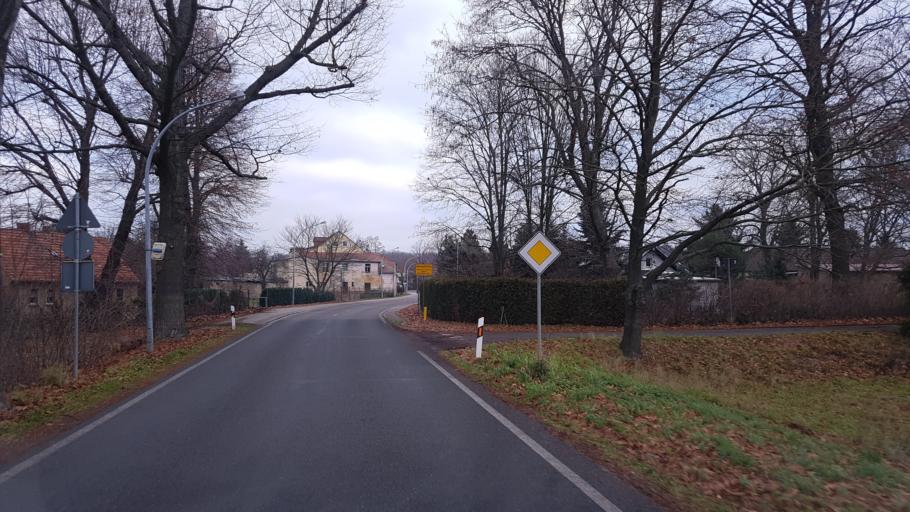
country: DE
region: Brandenburg
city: Schipkau
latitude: 51.5572
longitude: 13.8945
